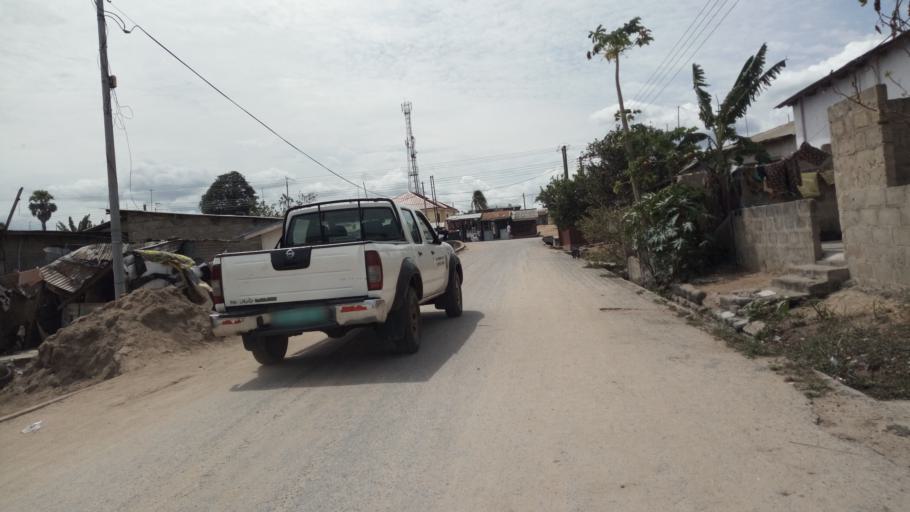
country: GH
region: Central
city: Winneba
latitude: 5.3471
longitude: -0.6206
